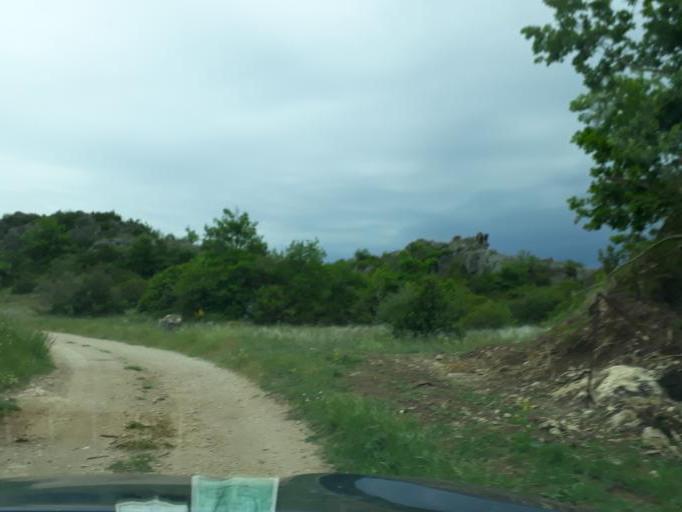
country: FR
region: Languedoc-Roussillon
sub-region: Departement de l'Herault
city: Lodeve
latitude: 43.8189
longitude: 3.2749
